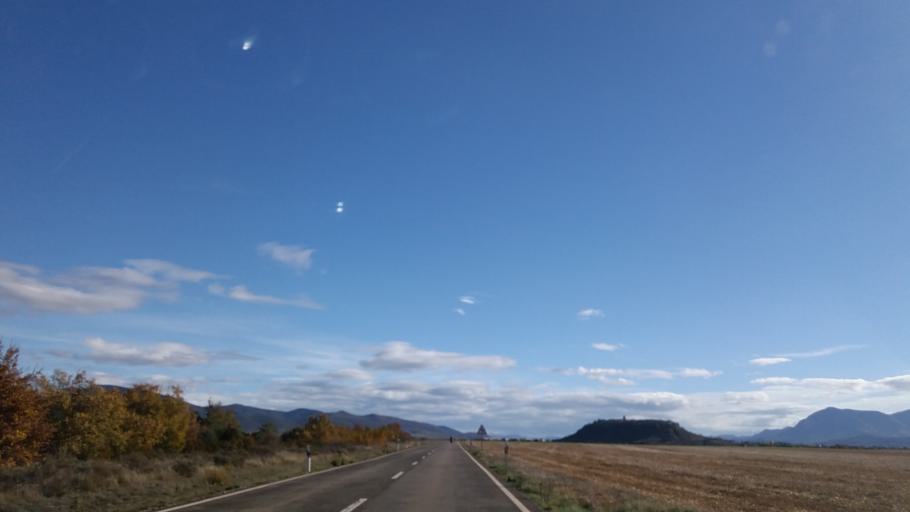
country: ES
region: Aragon
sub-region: Provincia de Zaragoza
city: Mianos
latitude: 42.6108
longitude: -0.8859
